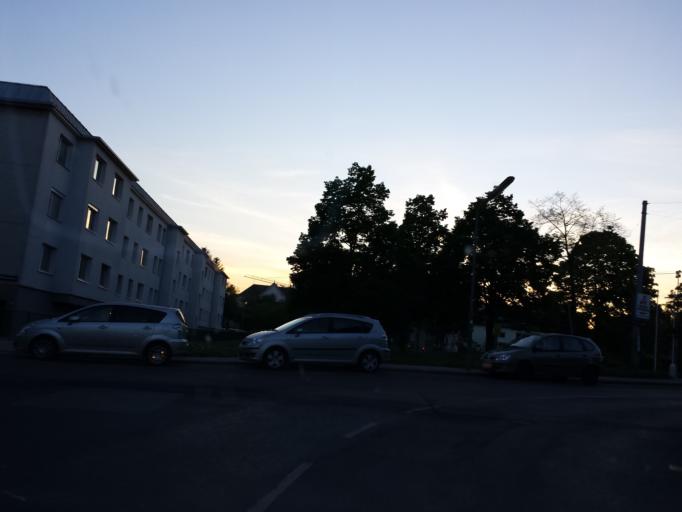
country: AT
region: Lower Austria
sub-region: Politischer Bezirk Modling
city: Perchtoldsdorf
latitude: 48.1470
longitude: 16.2858
